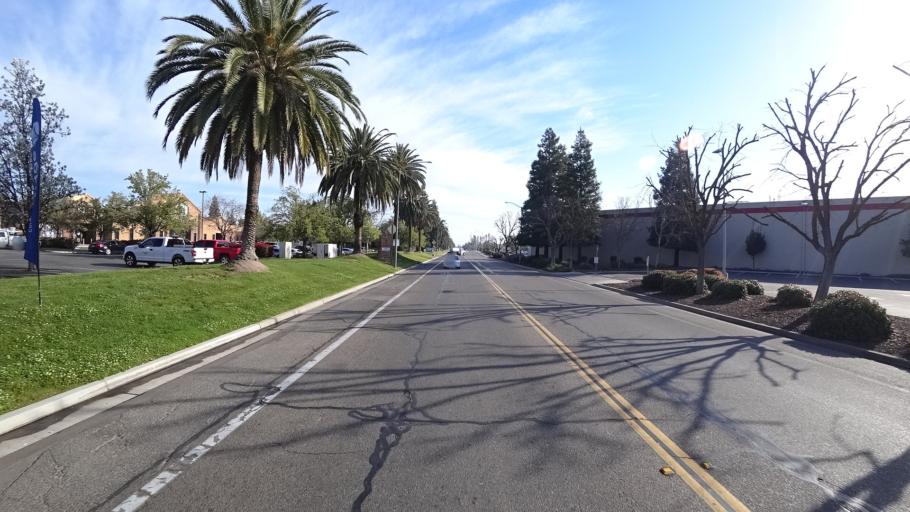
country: US
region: California
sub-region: Fresno County
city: West Park
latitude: 36.8101
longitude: -119.8753
